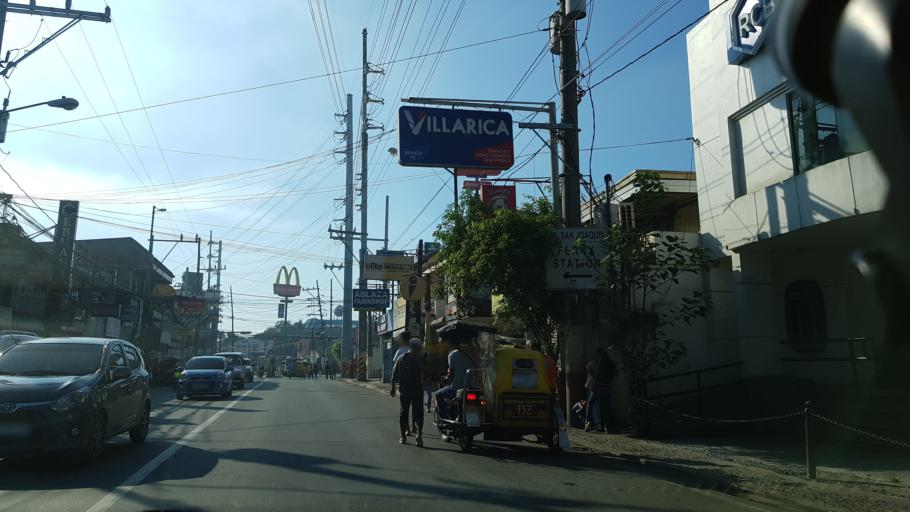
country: PH
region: Calabarzon
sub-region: Province of Rizal
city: Pateros
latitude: 14.5523
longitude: 121.0737
